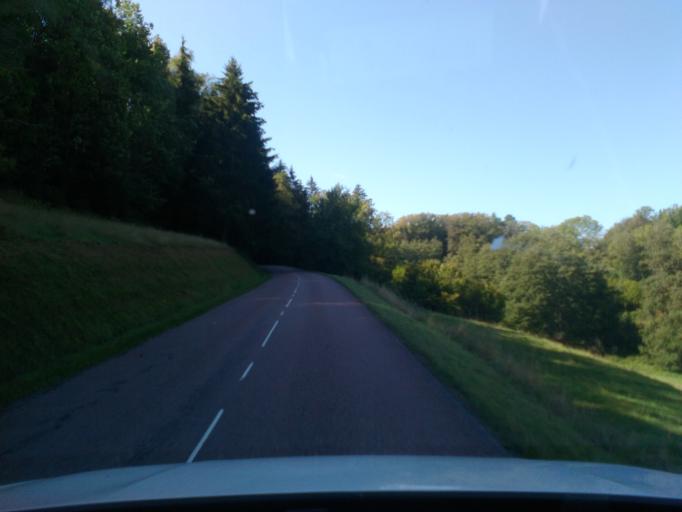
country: FR
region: Lorraine
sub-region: Departement des Vosges
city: Saint-Die-des-Vosges
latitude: 48.3317
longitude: 6.9854
